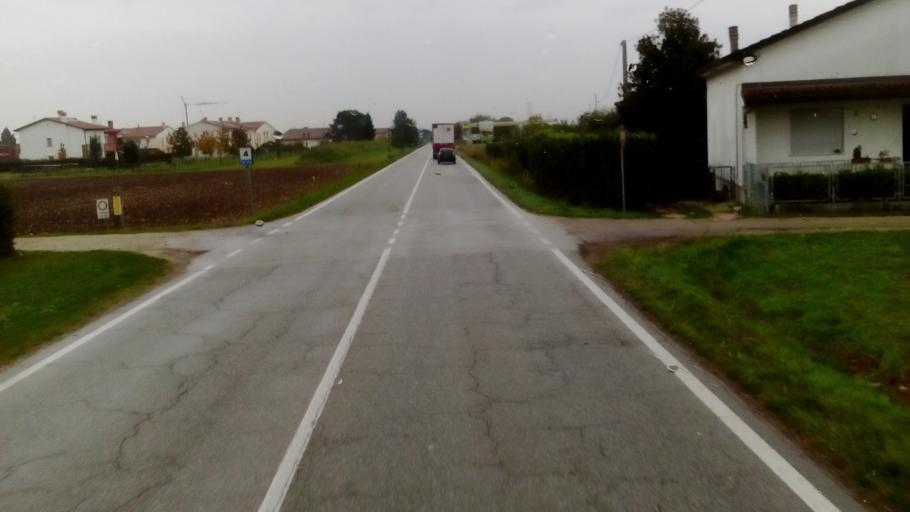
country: IT
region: Veneto
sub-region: Provincia di Vicenza
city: Breganze
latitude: 45.6866
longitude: 11.5642
